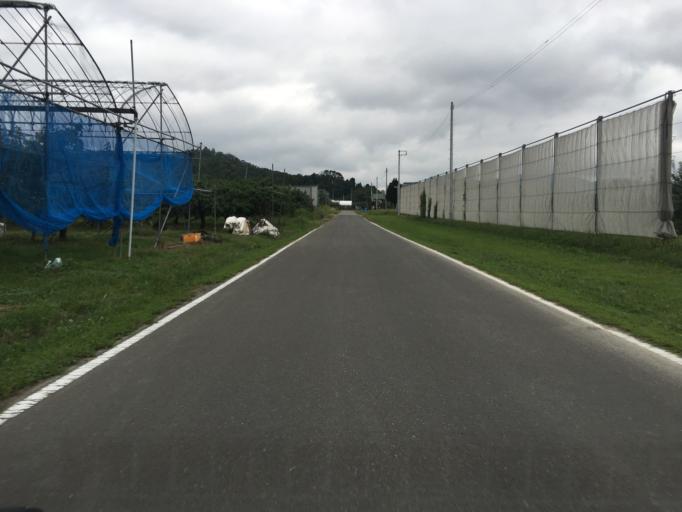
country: JP
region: Fukushima
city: Fukushima-shi
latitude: 37.8107
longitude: 140.4295
